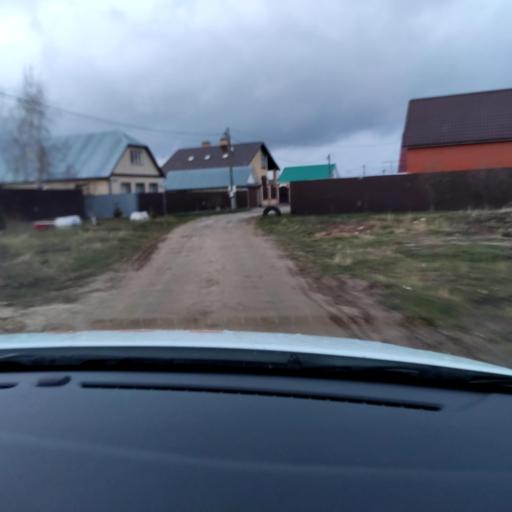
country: RU
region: Tatarstan
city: Stolbishchi
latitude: 55.6924
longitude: 49.1540
